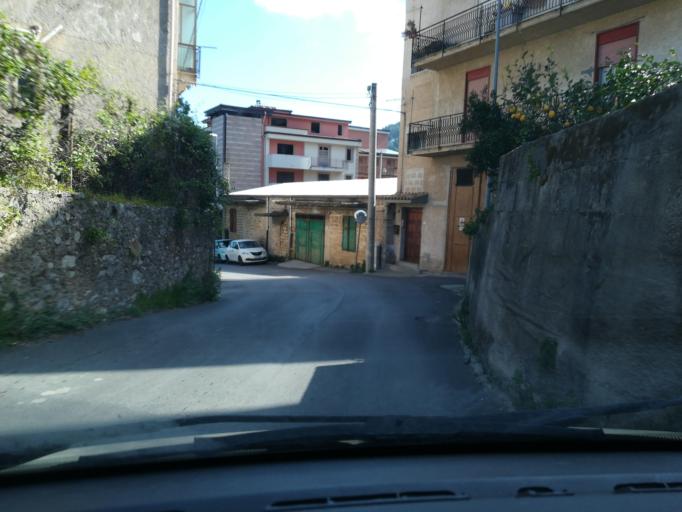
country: IT
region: Sicily
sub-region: Palermo
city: Altofonte
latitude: 38.0428
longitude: 13.2927
